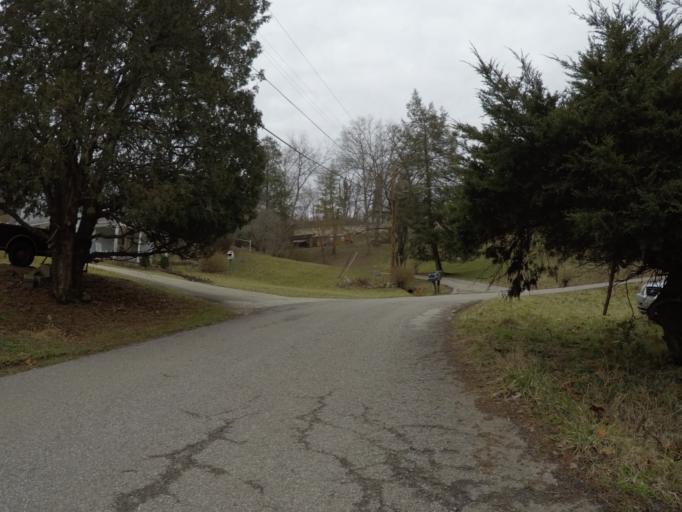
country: US
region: Ohio
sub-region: Lawrence County
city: Burlington
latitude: 38.3925
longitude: -82.5177
